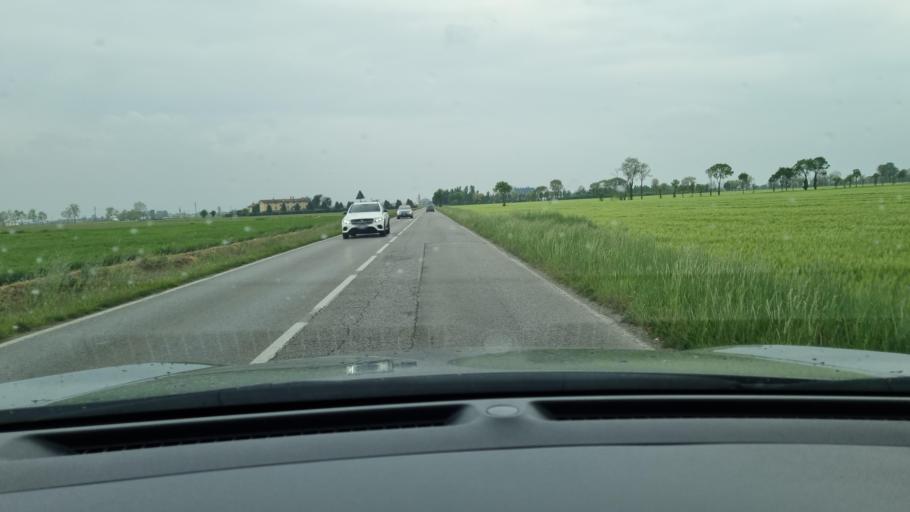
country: IT
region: Lombardy
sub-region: Provincia di Bergamo
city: Cavernago
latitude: 45.6151
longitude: 9.7715
